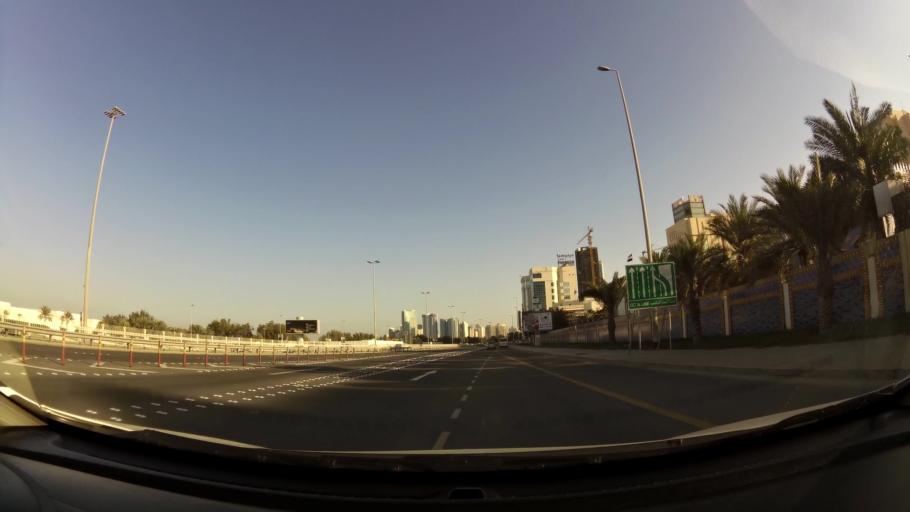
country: BH
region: Muharraq
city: Al Muharraq
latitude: 26.2388
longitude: 50.5958
